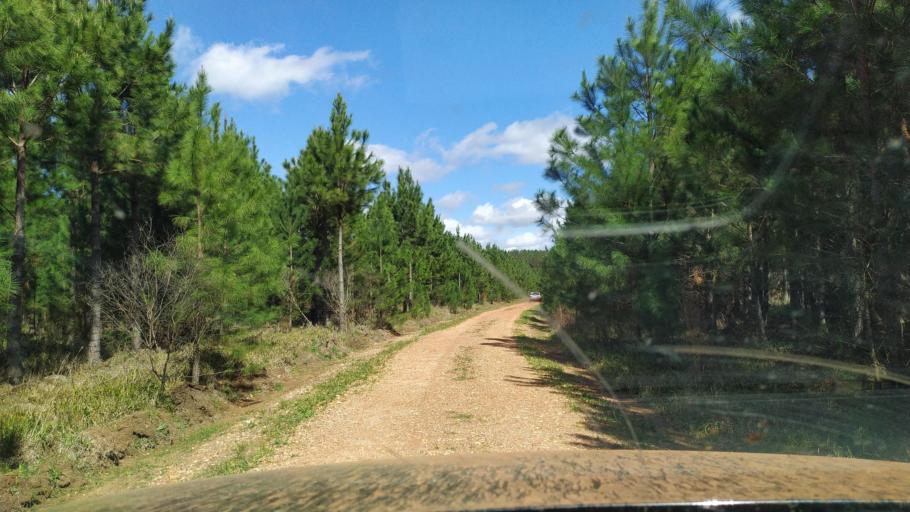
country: AR
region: Corrientes
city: Santo Tome
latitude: -28.4620
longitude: -55.9879
